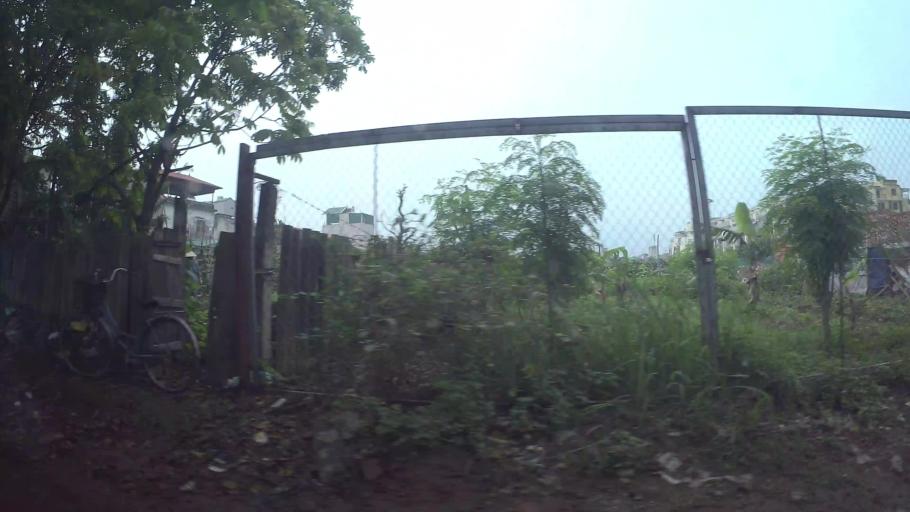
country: VN
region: Ha Noi
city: Van Dien
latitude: 20.9738
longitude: 105.8709
